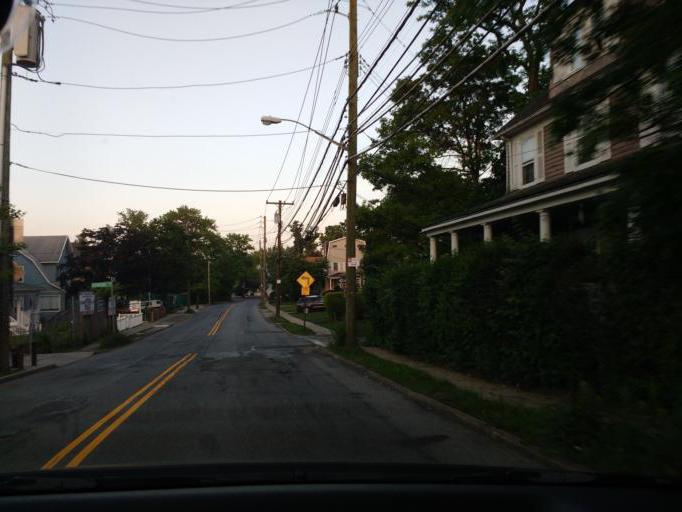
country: US
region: New York
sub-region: Richmond County
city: Staten Island
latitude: 40.5516
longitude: -74.1477
